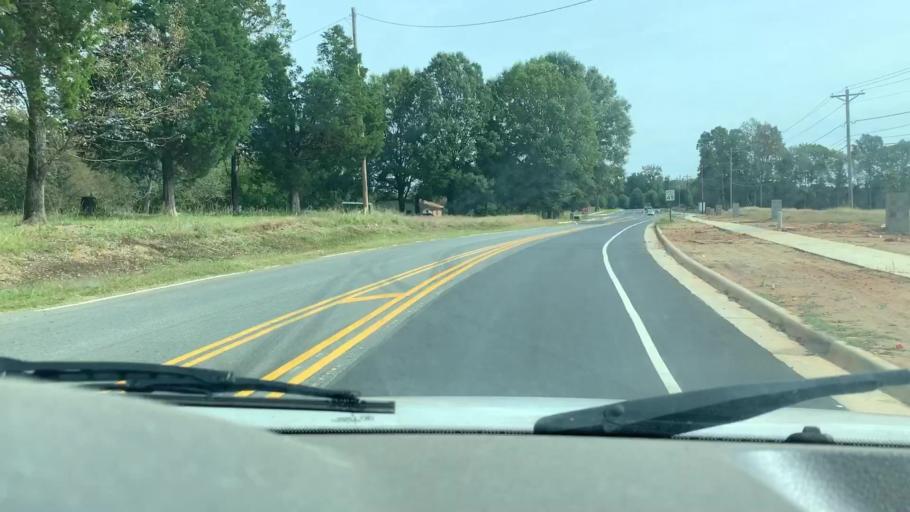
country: US
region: North Carolina
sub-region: Mecklenburg County
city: Huntersville
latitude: 35.4133
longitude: -80.8177
